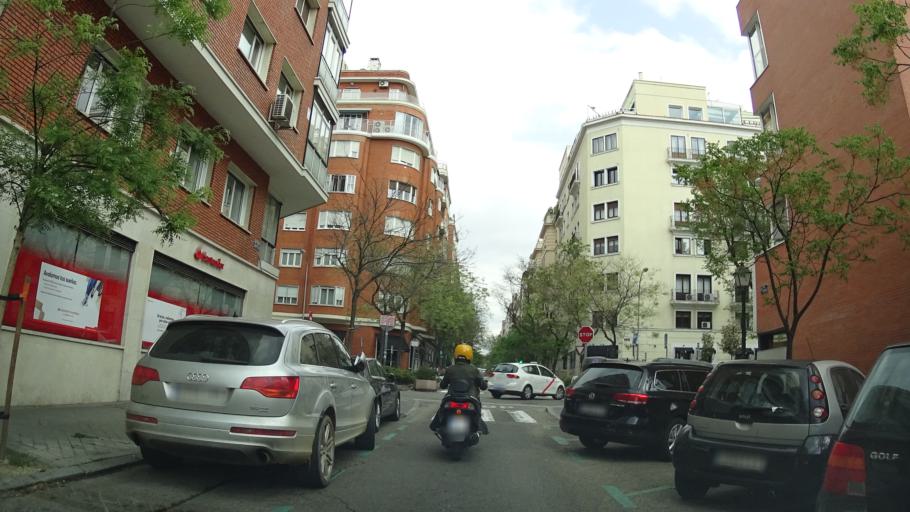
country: ES
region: Madrid
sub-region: Provincia de Madrid
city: Salamanca
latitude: 40.4324
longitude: -3.6809
